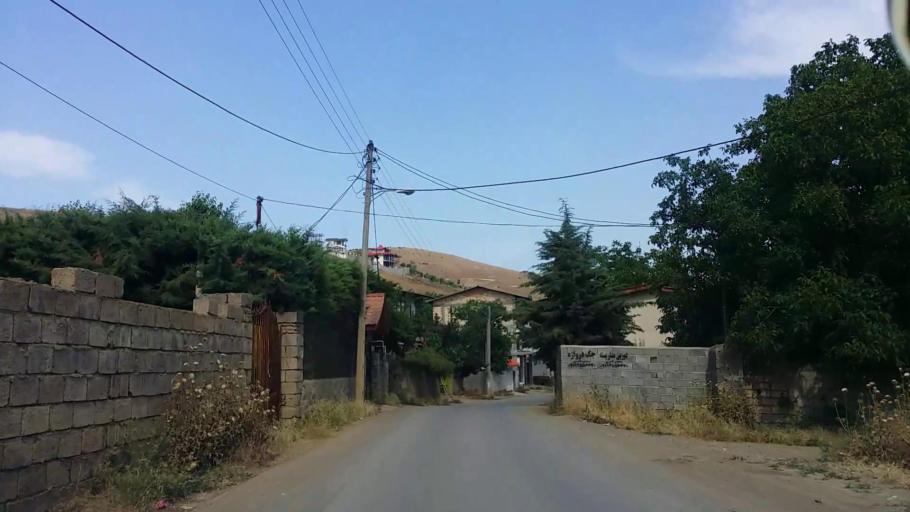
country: IR
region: Mazandaran
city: Chalus
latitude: 36.5155
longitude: 51.2508
